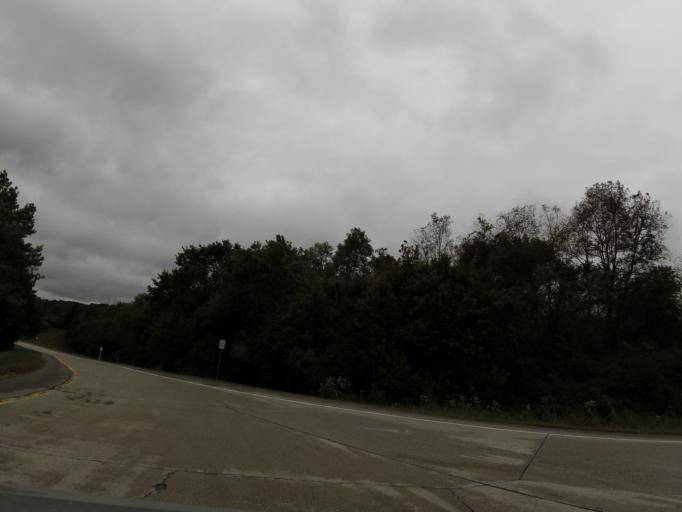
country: US
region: Tennessee
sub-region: Loudon County
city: Loudon
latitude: 35.7849
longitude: -84.3459
